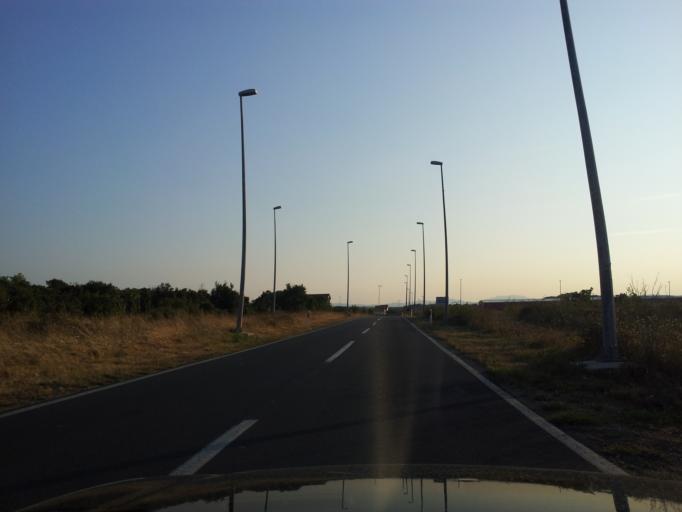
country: HR
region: Zadarska
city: Polaca
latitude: 44.0028
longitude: 15.5023
